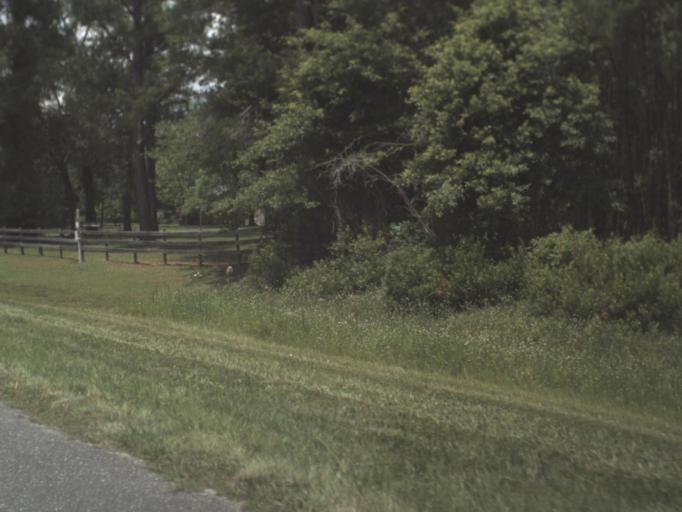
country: US
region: Florida
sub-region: Columbia County
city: Watertown
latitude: 30.1582
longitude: -82.5635
